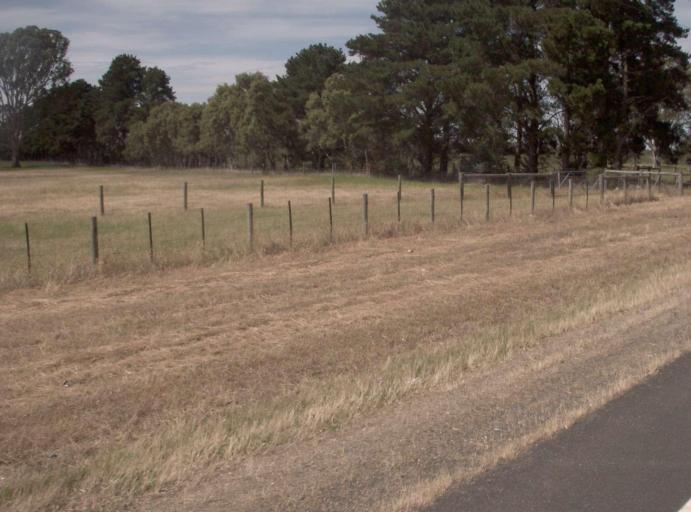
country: AU
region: Victoria
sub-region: Wellington
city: Sale
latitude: -37.9270
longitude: 147.2171
